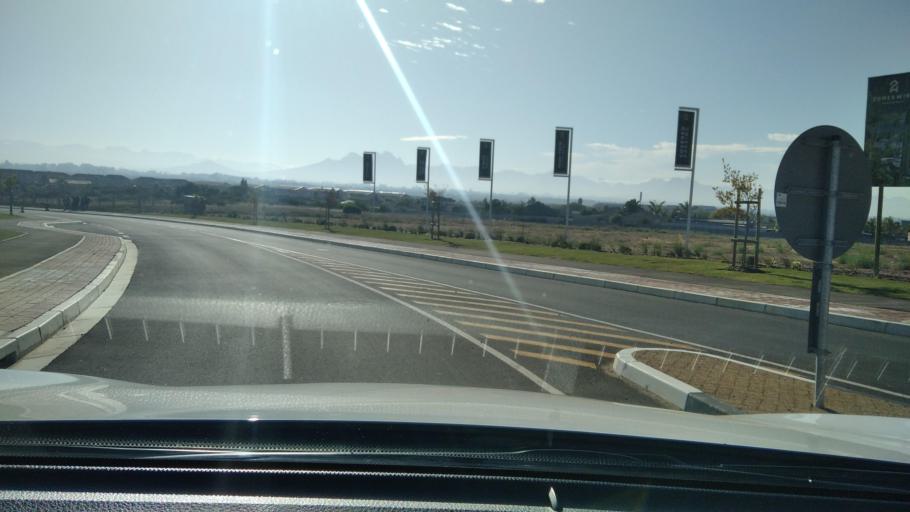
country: ZA
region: Western Cape
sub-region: City of Cape Town
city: Kraaifontein
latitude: -33.8115
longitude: 18.6894
